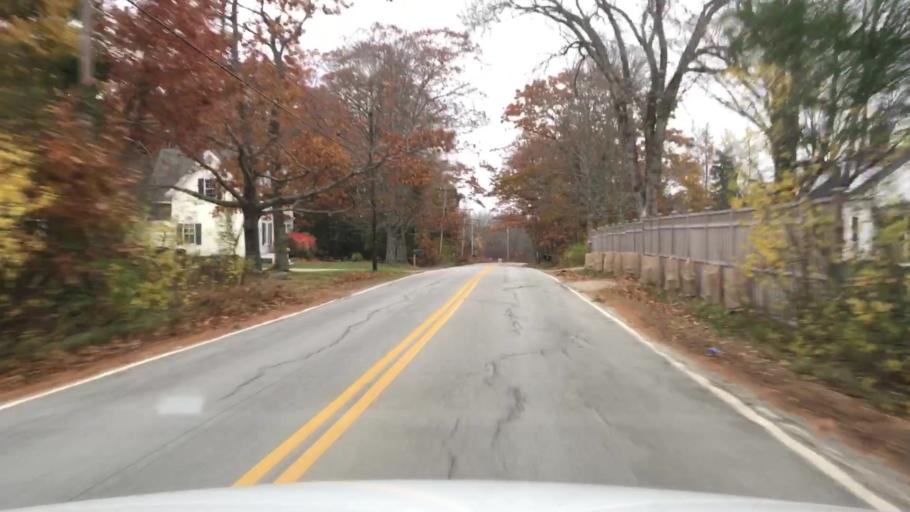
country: US
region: Maine
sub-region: Hancock County
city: Sedgwick
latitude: 44.2710
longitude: -68.5654
